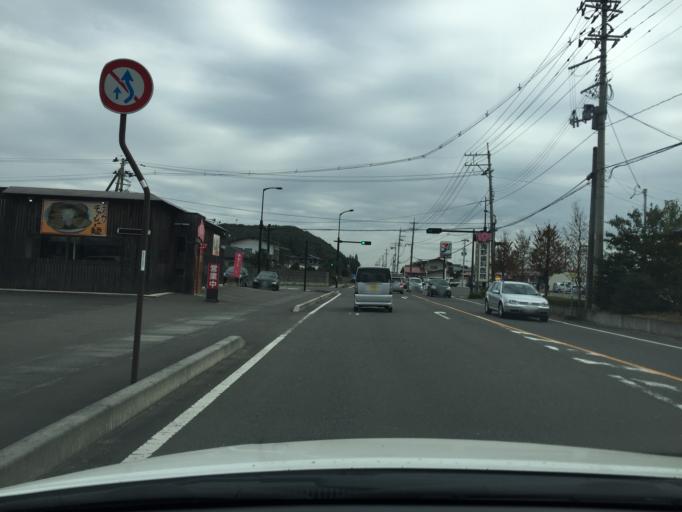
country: JP
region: Tochigi
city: Kuroiso
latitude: 37.1334
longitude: 140.1695
